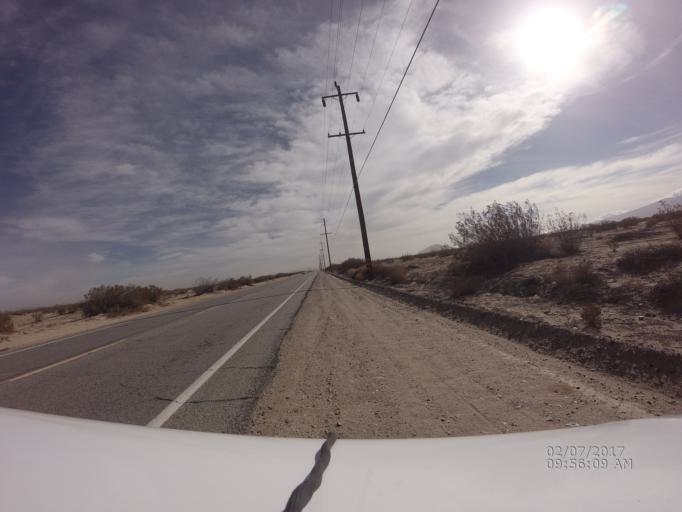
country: US
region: California
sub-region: Los Angeles County
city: Lake Los Angeles
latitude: 34.5800
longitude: -117.7883
